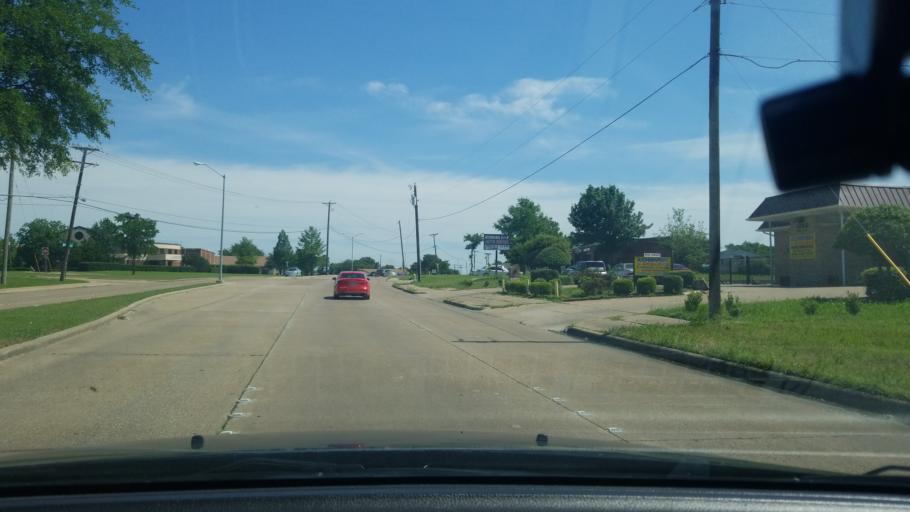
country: US
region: Texas
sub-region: Dallas County
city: Mesquite
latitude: 32.7782
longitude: -96.5970
